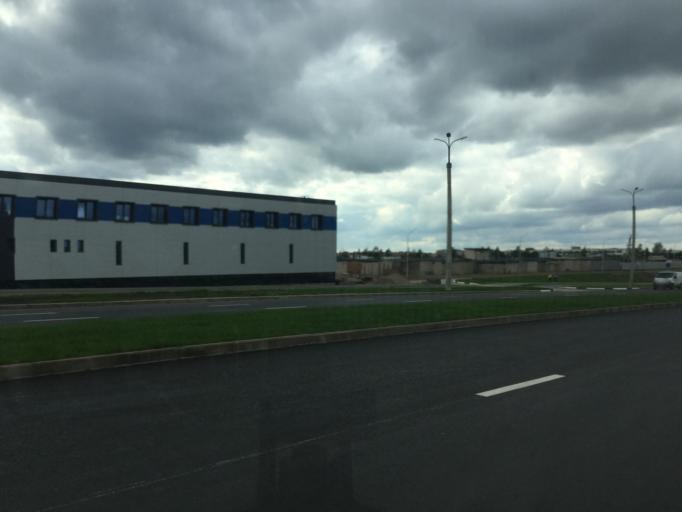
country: BY
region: Vitebsk
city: Vitebsk
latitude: 55.1670
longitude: 30.2527
